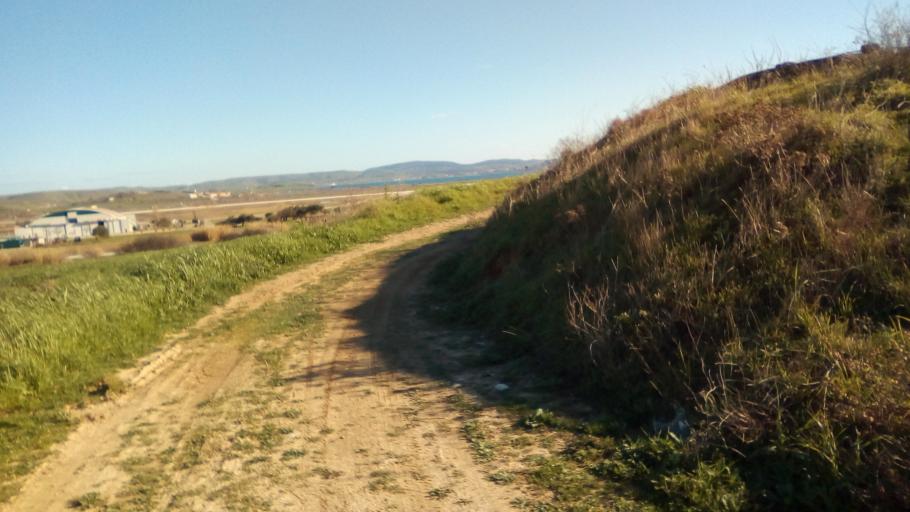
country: GR
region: North Aegean
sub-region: Nomos Lesvou
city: Myrina
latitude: 39.9319
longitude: 25.2366
